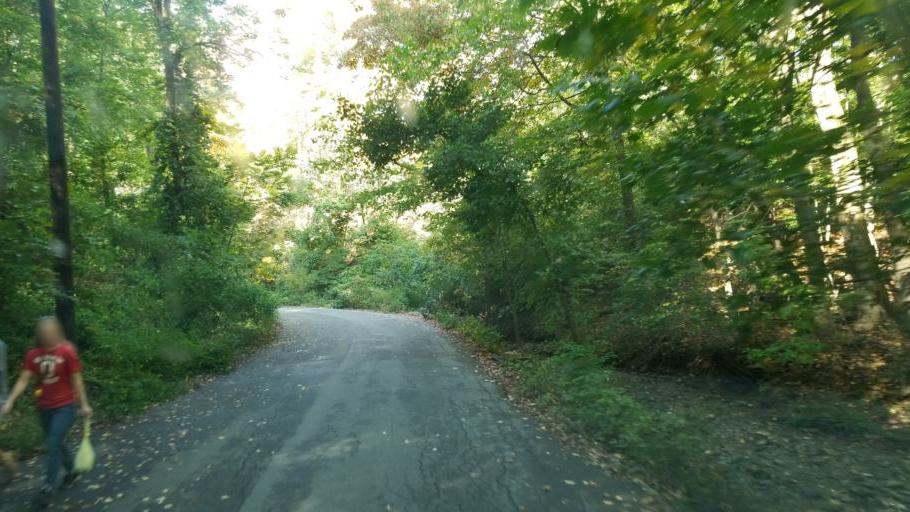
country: US
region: Ohio
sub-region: Franklin County
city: Grandview Heights
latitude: 40.0292
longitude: -83.0034
